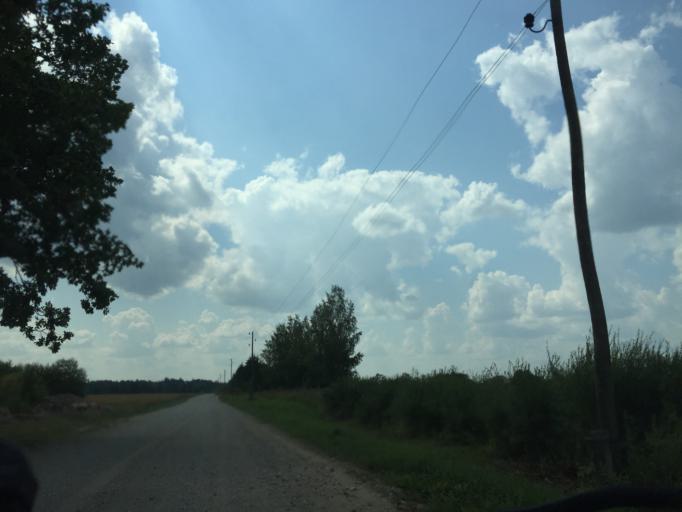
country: LT
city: Zagare
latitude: 56.3833
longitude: 23.1806
